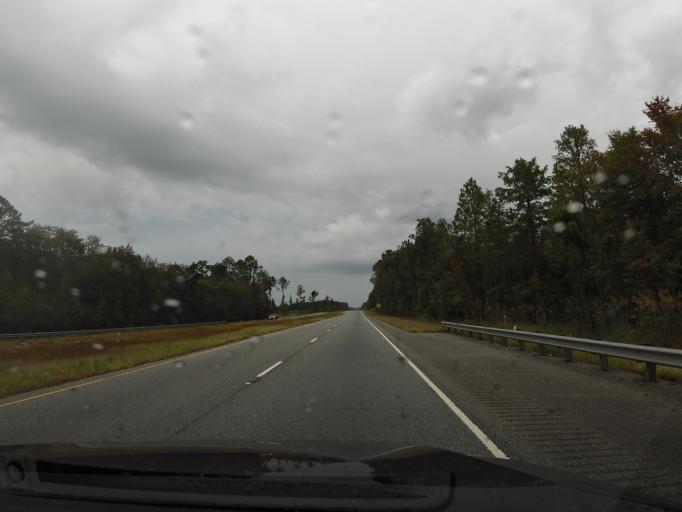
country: US
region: Georgia
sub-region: Wayne County
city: Jesup
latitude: 31.5291
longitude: -81.7880
